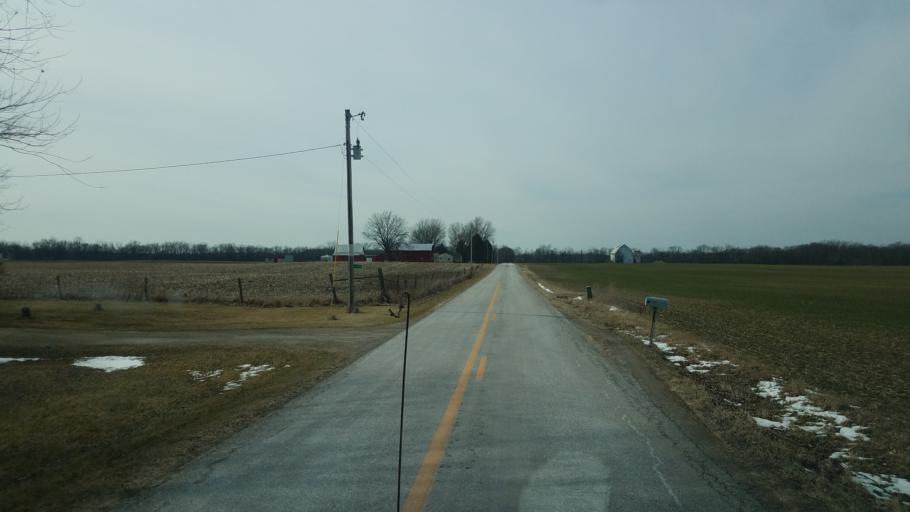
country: US
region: Ohio
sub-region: Marion County
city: Prospect
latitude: 40.3657
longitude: -83.1752
